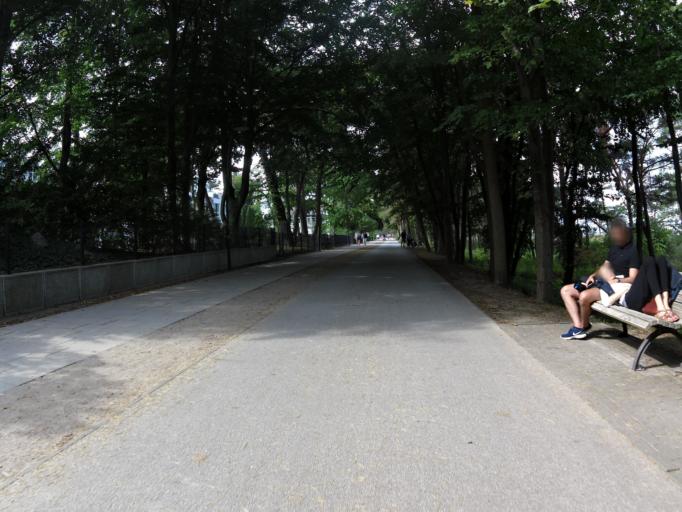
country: DE
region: Mecklenburg-Vorpommern
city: Seebad Heringsdorf
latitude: 53.9640
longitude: 14.1572
